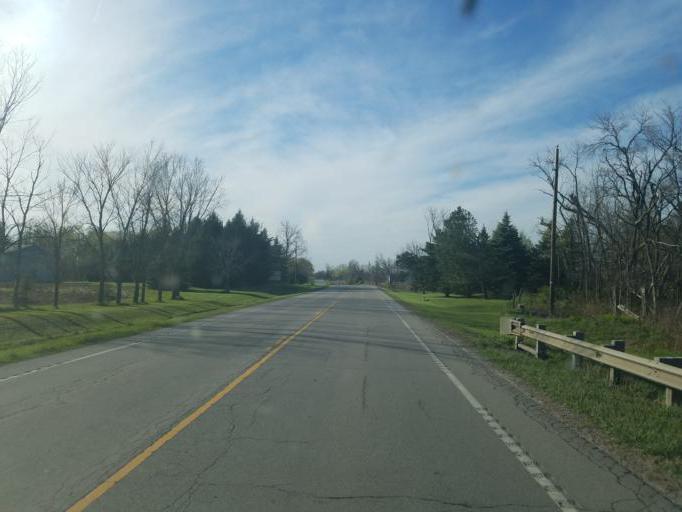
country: US
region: Ohio
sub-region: Huron County
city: New London
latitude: 41.0339
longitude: -82.4208
